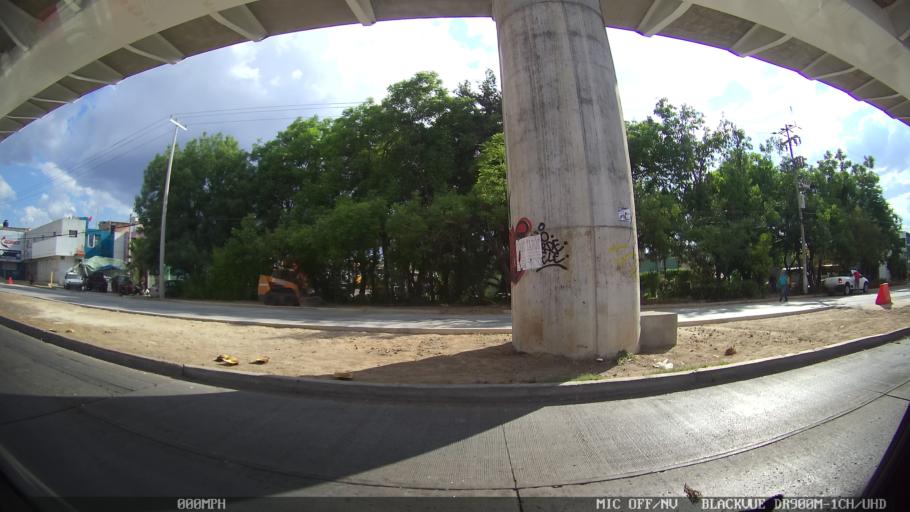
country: MX
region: Jalisco
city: Tlaquepaque
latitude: 20.6399
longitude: -103.3014
